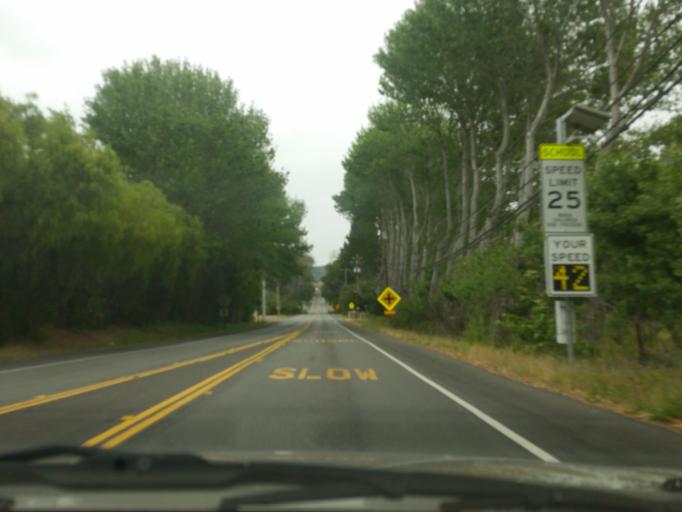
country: US
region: California
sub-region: San Luis Obispo County
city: Avila Beach
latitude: 35.1939
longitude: -120.7168
